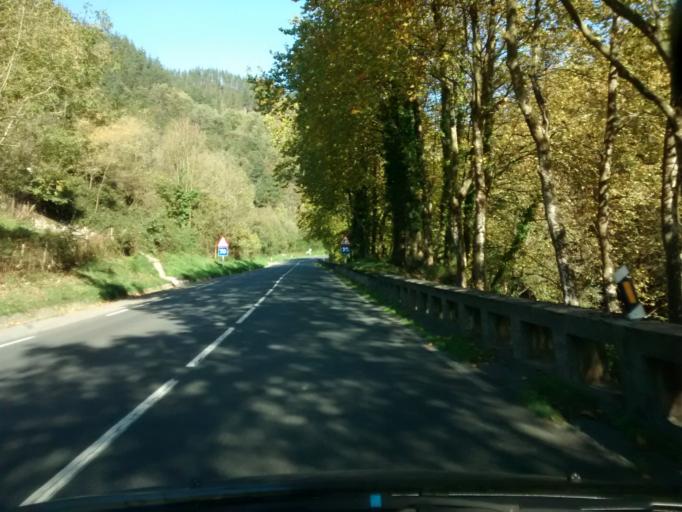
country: ES
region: Basque Country
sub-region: Provincia de Guipuzcoa
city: Mendaro
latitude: 43.2402
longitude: -2.3983
